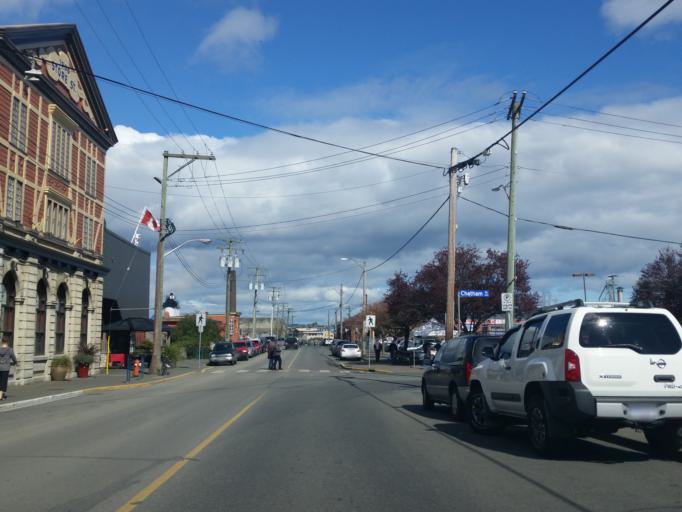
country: CA
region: British Columbia
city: Victoria
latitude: 48.4307
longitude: -123.3696
